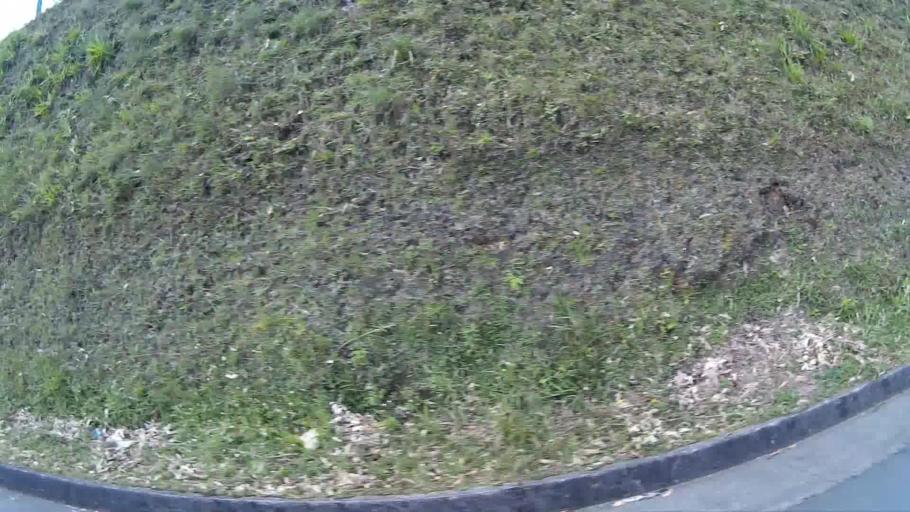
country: CO
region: Quindio
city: Salento
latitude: 4.6773
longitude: -75.6024
